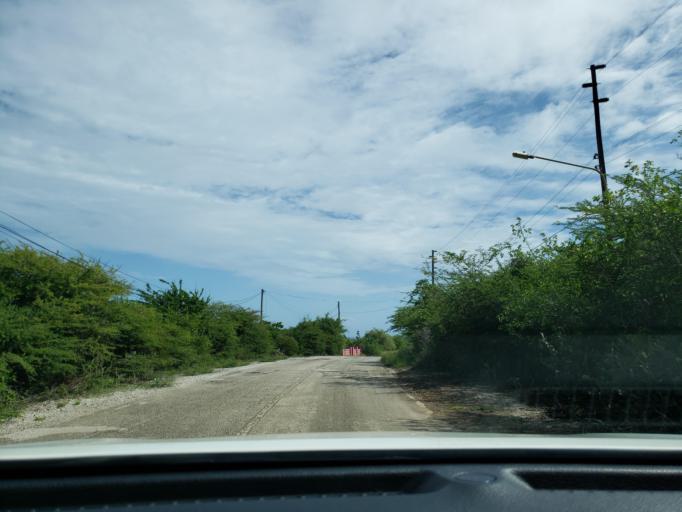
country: CW
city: Barber
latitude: 12.3145
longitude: -69.0905
